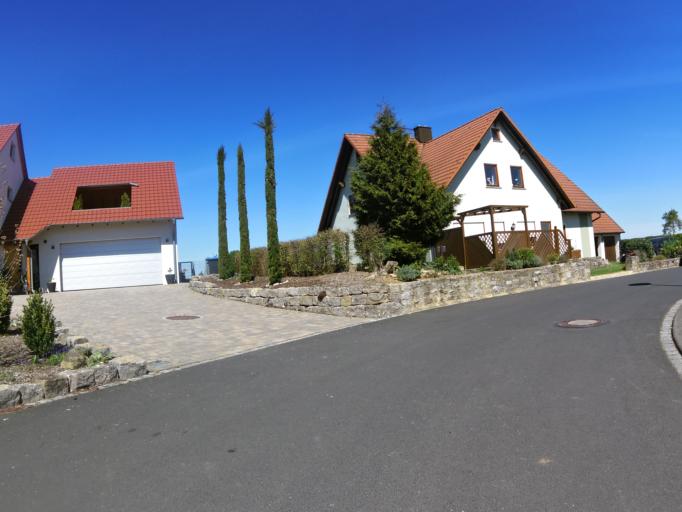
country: DE
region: Bavaria
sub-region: Regierungsbezirk Unterfranken
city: Biebelried
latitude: 49.7981
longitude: 10.0886
